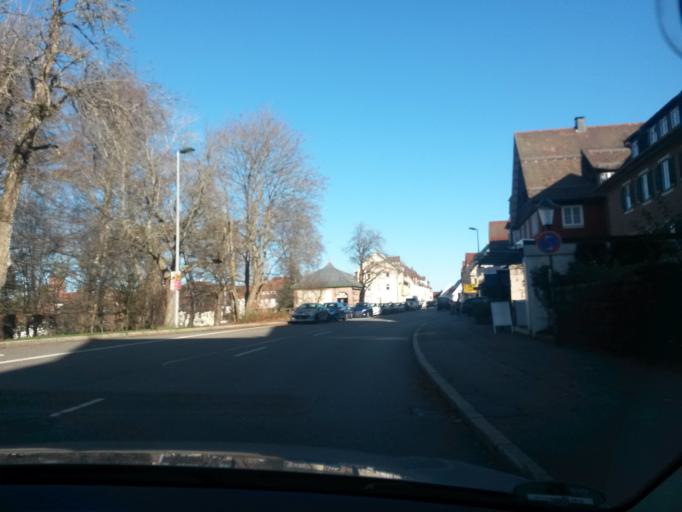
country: DE
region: Baden-Wuerttemberg
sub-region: Karlsruhe Region
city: Freudenstadt
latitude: 48.4598
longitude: 8.4091
